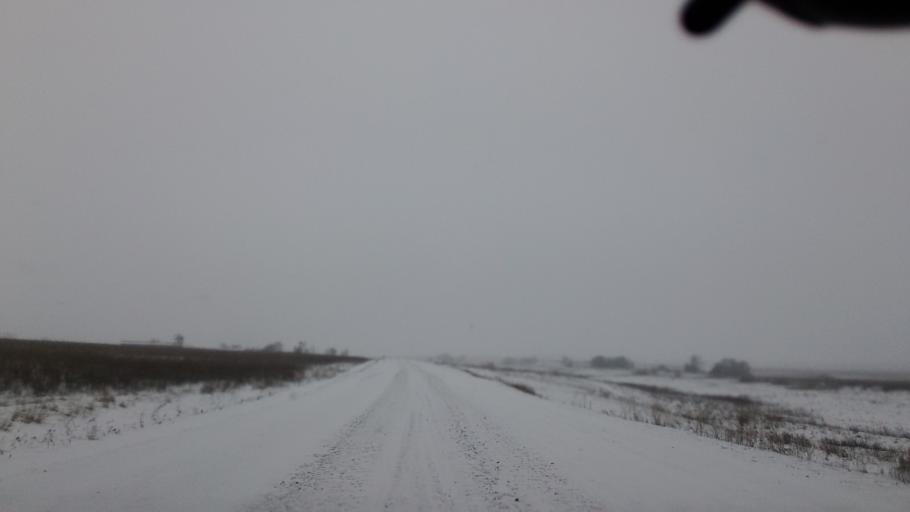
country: RU
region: Tula
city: Volovo
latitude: 53.6829
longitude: 37.9307
